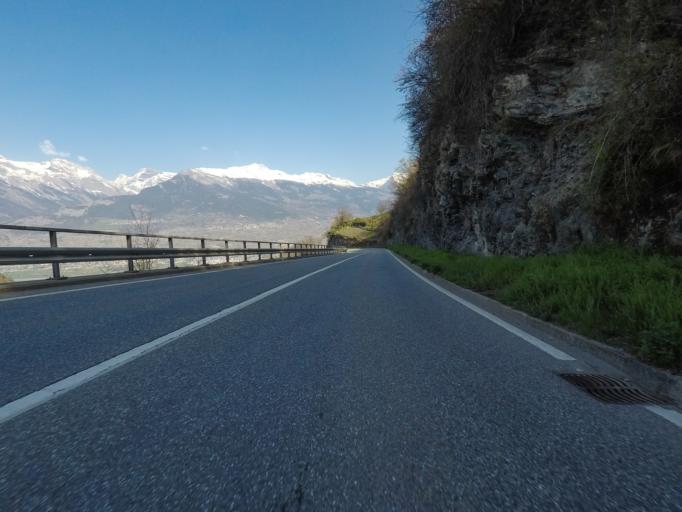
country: CH
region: Valais
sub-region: Conthey District
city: Basse-Nendaz
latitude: 46.1953
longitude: 7.3227
